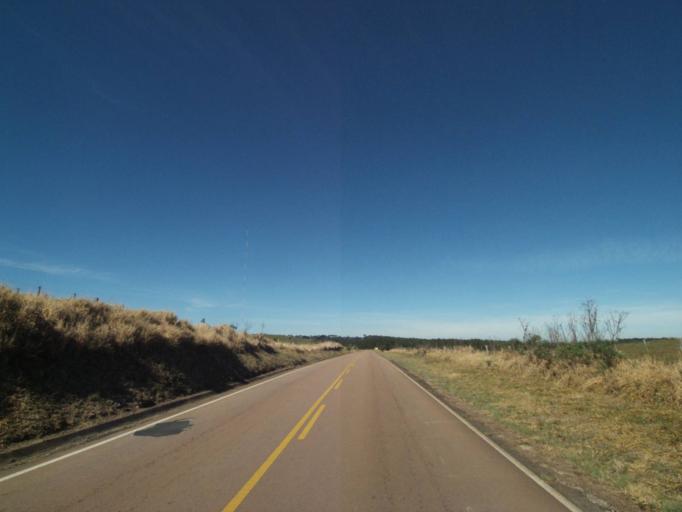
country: BR
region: Parana
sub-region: Tibagi
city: Tibagi
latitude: -24.6450
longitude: -50.2325
